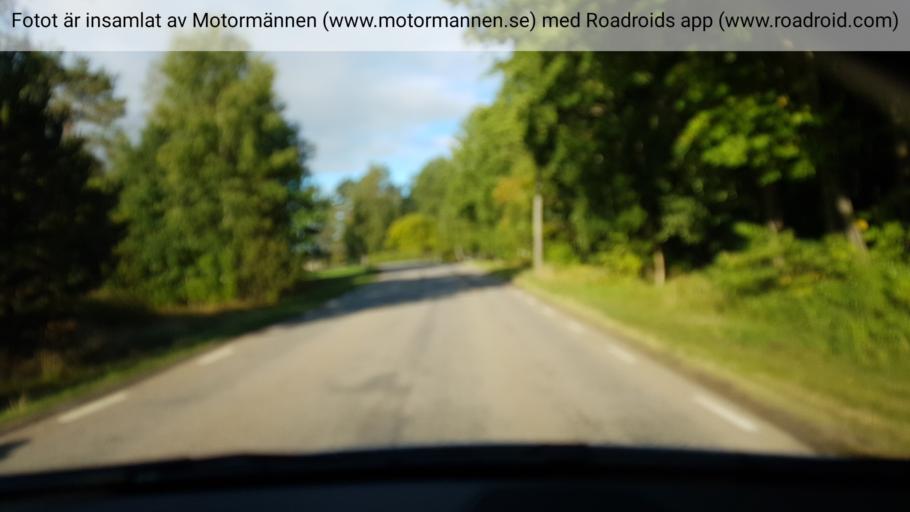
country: SE
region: Vaestra Goetaland
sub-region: Gotene Kommun
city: Goetene
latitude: 58.5350
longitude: 13.5412
